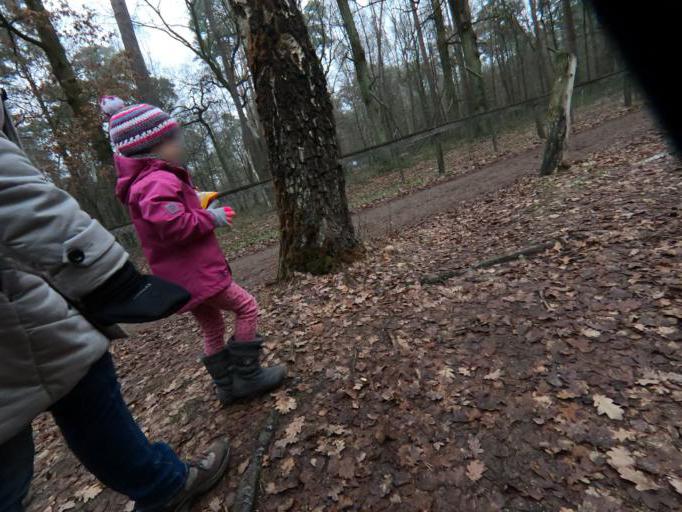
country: DE
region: Hesse
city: Obertshausen
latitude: 50.0794
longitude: 8.9041
